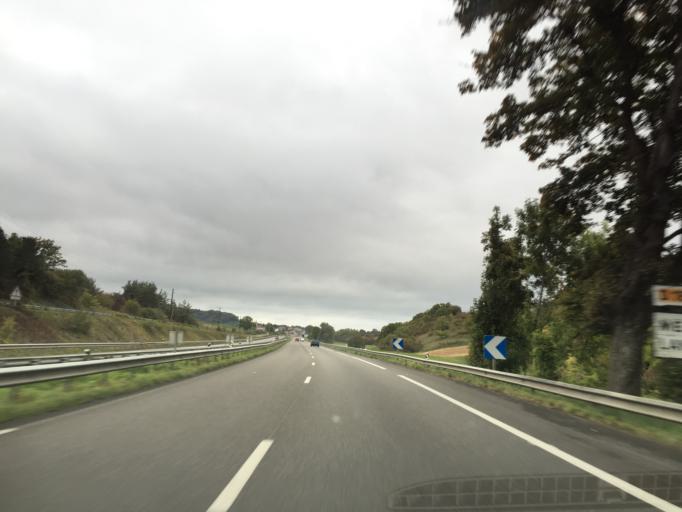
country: FR
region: Lorraine
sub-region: Departement de la Meuse
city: Vacon
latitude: 48.6947
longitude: 5.5481
